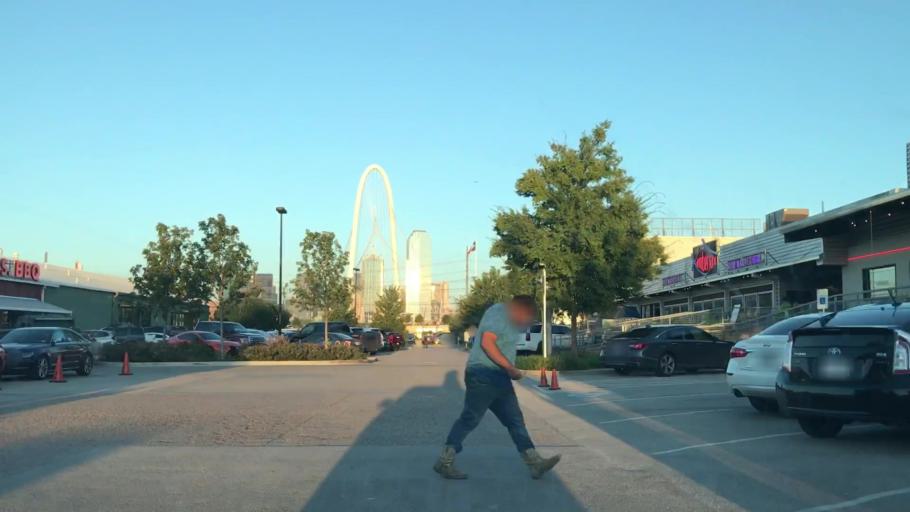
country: US
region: Texas
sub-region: Dallas County
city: Dallas
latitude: 32.7796
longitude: -96.8290
